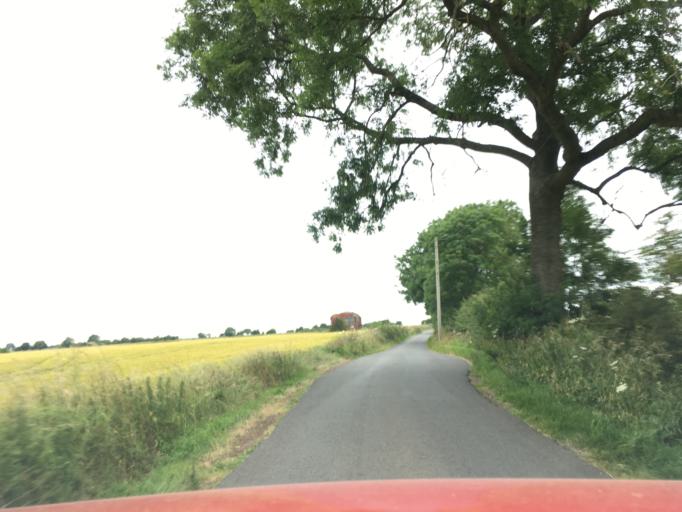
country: GB
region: England
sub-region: Gloucestershire
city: Shipton Village
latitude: 51.8921
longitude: -1.9140
